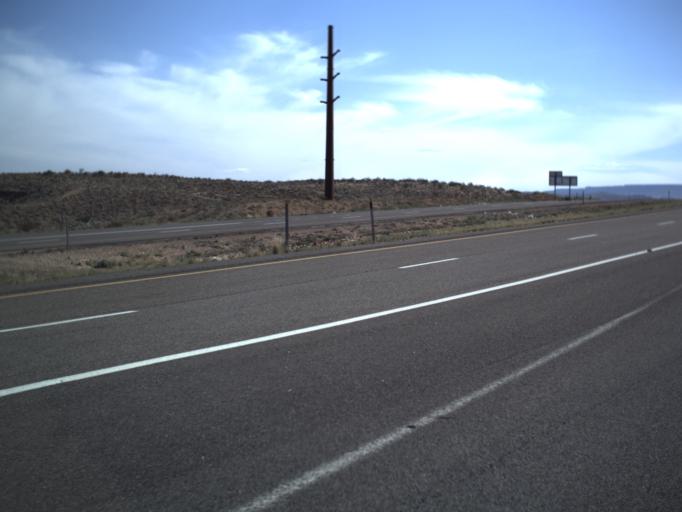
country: US
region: Utah
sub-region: Washington County
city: Saint George
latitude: 37.0004
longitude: -113.5562
